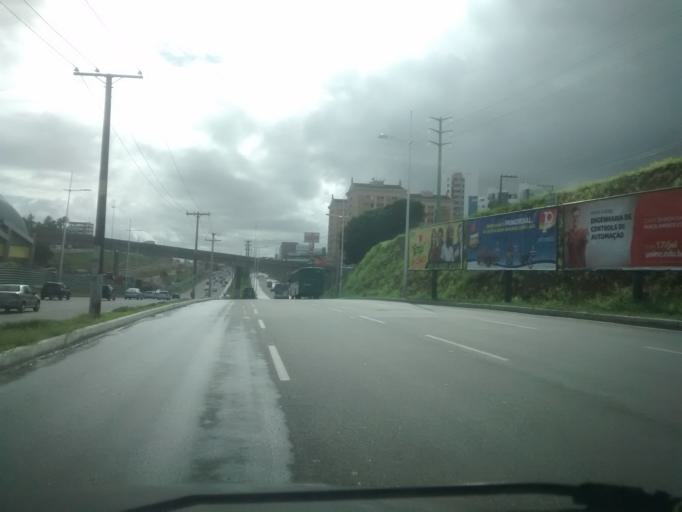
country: BR
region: Bahia
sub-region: Salvador
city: Salvador
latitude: -12.9658
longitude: -38.4366
